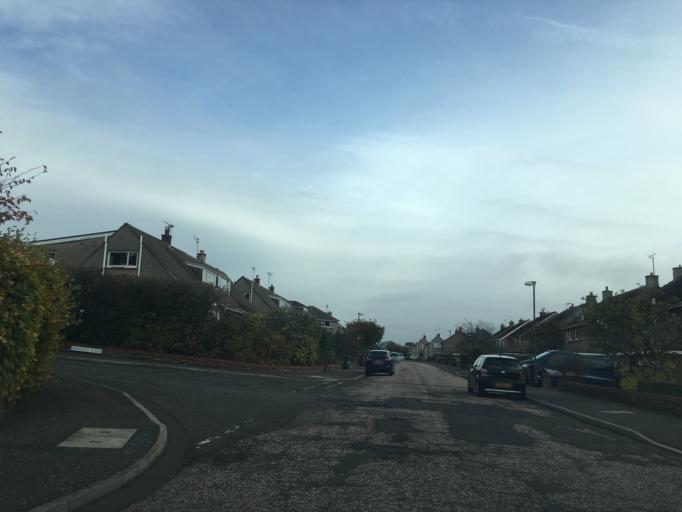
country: GB
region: Scotland
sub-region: Edinburgh
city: Colinton
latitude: 55.8992
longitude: -3.2115
